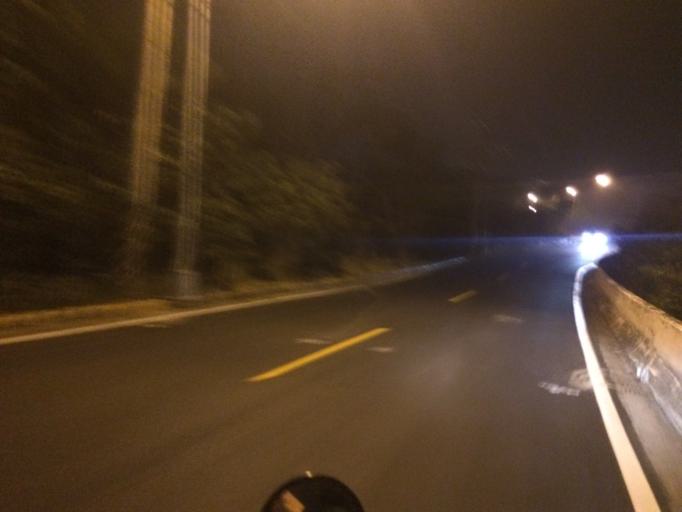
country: TW
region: Taiwan
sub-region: Hsinchu
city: Hsinchu
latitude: 24.7276
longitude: 120.9009
